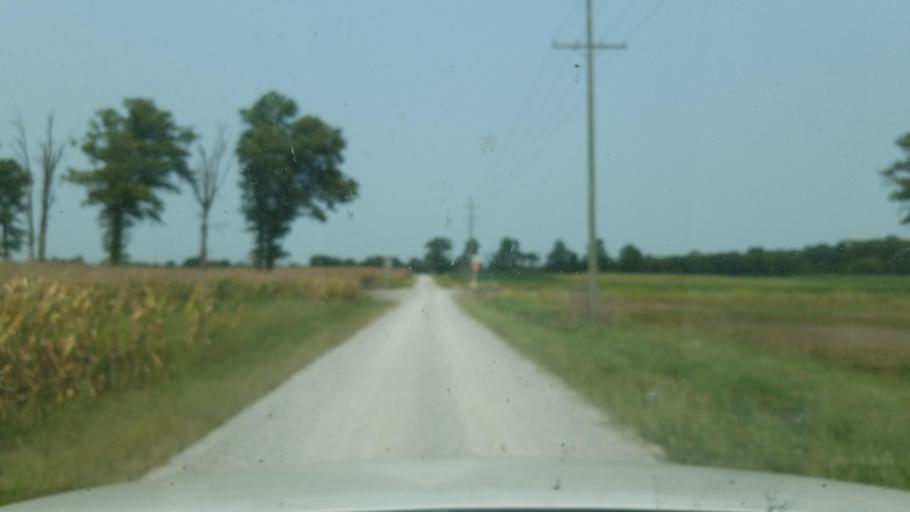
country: US
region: Illinois
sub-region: Saline County
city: Eldorado
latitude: 37.8158
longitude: -88.5167
